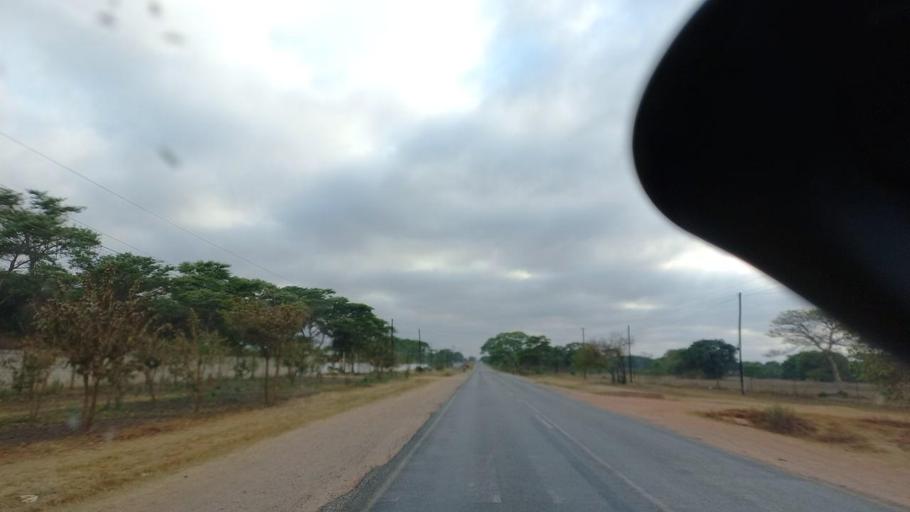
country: ZM
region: Lusaka
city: Chongwe
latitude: -15.3474
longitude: 28.5042
